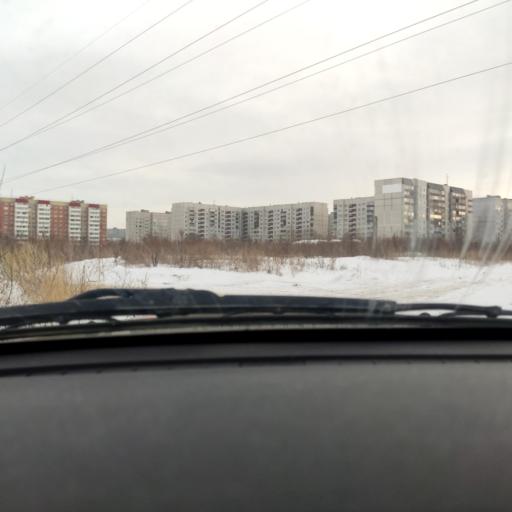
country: RU
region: Samara
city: Tol'yatti
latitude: 53.5438
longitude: 49.3972
